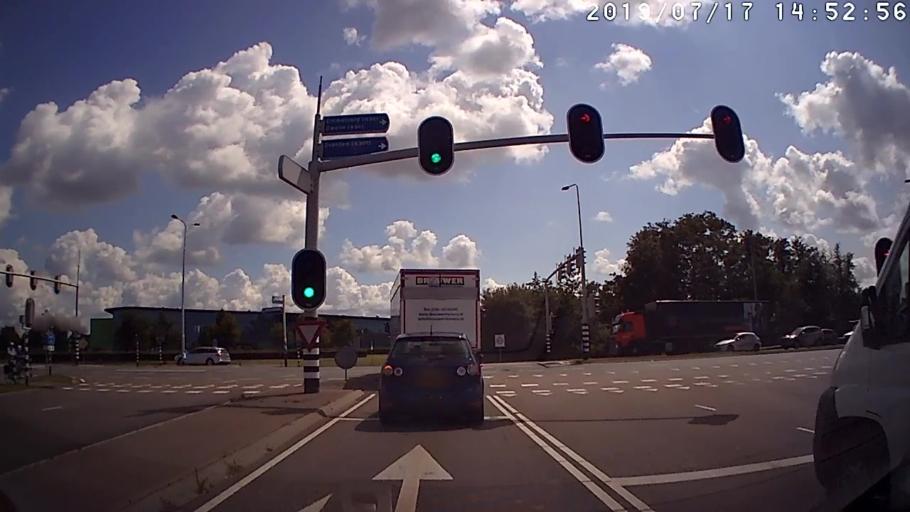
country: NL
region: Overijssel
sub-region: Gemeente Kampen
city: Kampen
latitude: 52.5561
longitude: 5.8859
